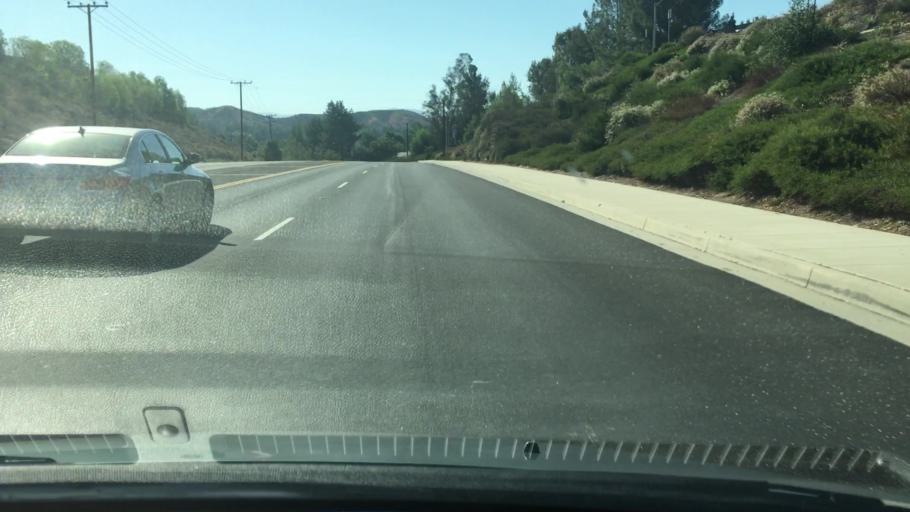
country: US
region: California
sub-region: Los Angeles County
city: Santa Clarita
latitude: 34.4610
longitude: -118.5413
